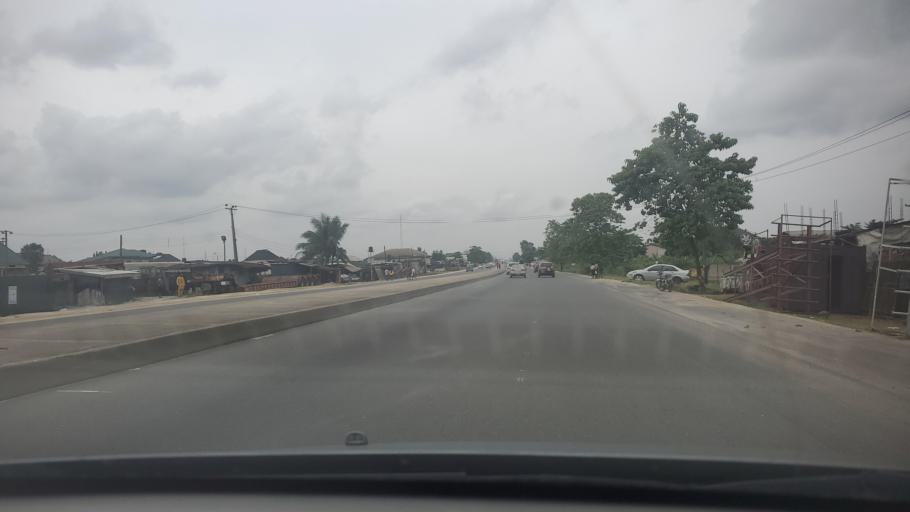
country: NG
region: Rivers
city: Port Harcourt
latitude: 4.8710
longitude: 6.9663
